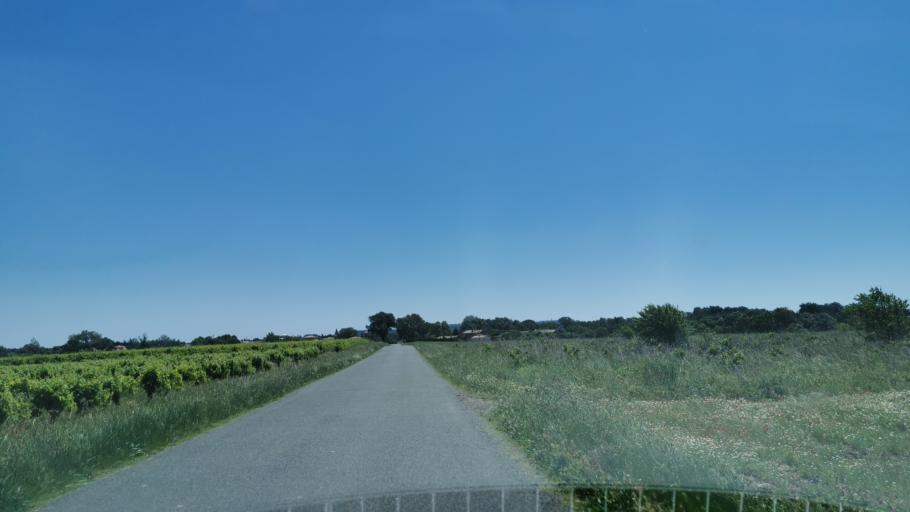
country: FR
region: Languedoc-Roussillon
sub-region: Departement de l'Aude
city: Ginestas
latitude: 43.2464
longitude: 2.8789
